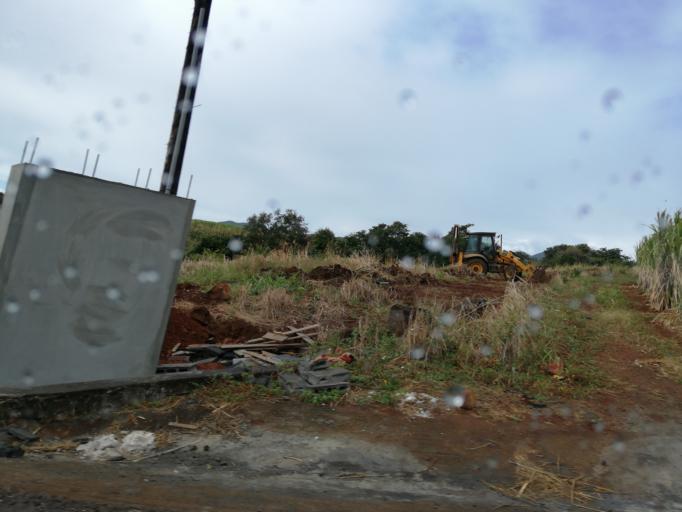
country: MU
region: Pamplemousses
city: Long Mountain
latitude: -20.1255
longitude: 57.5666
